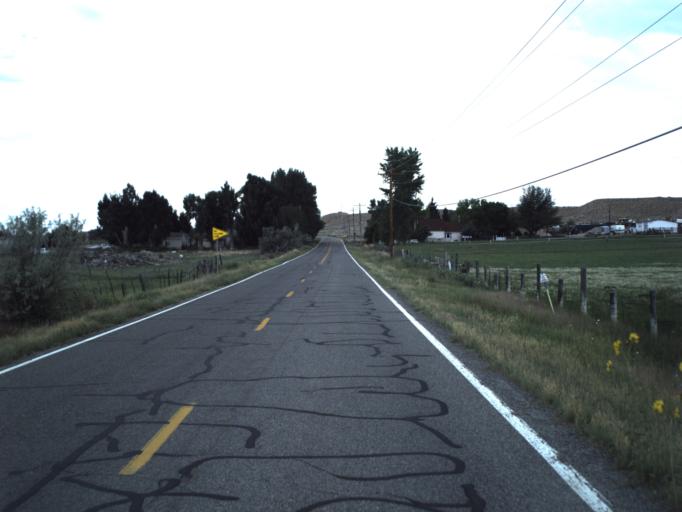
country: US
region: Utah
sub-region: Emery County
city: Huntington
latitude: 39.3773
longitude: -110.8524
